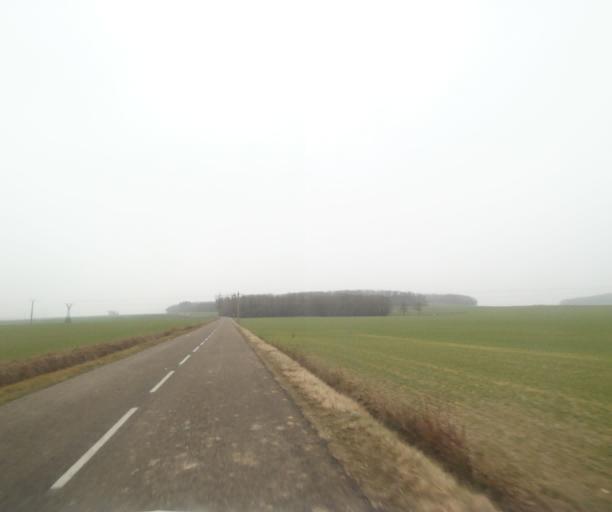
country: FR
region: Champagne-Ardenne
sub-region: Departement de la Haute-Marne
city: Bienville
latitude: 48.5222
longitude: 5.0474
